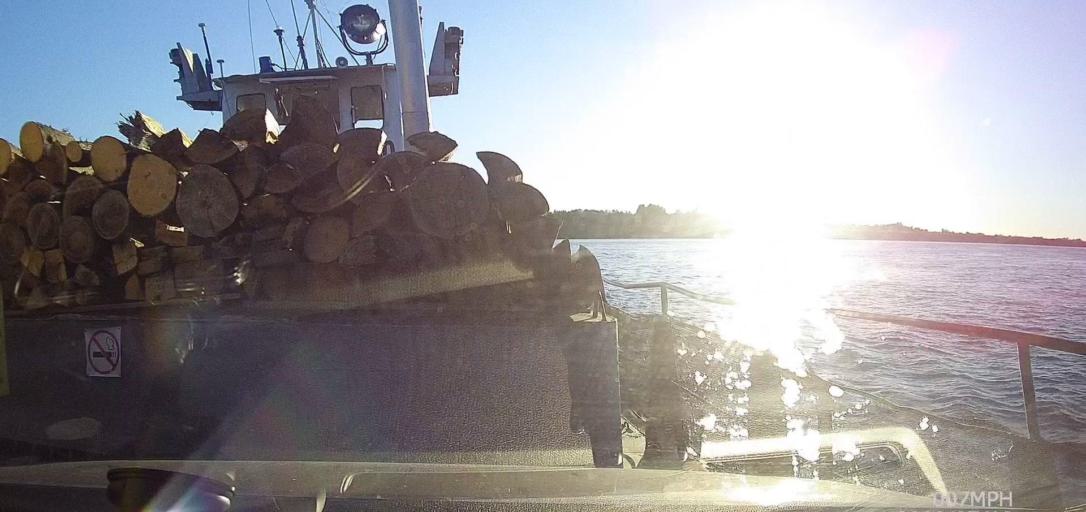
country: RU
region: Arkhangelskaya
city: Lukovetskiy
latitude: 64.1581
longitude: 41.9139
